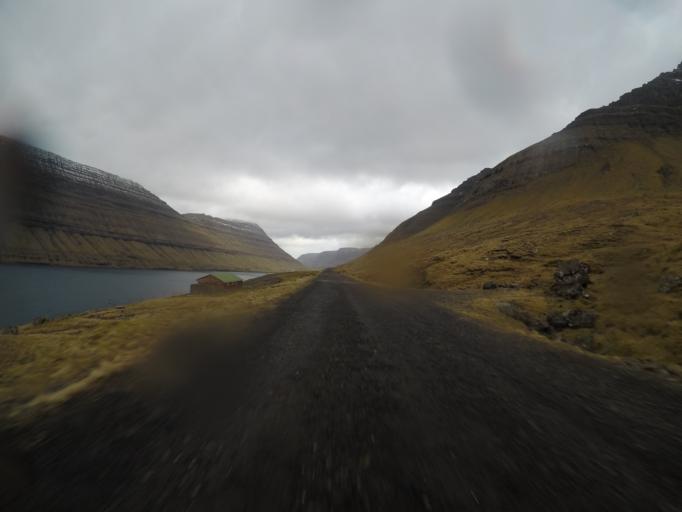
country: FO
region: Nordoyar
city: Klaksvik
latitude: 62.3179
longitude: -6.5569
